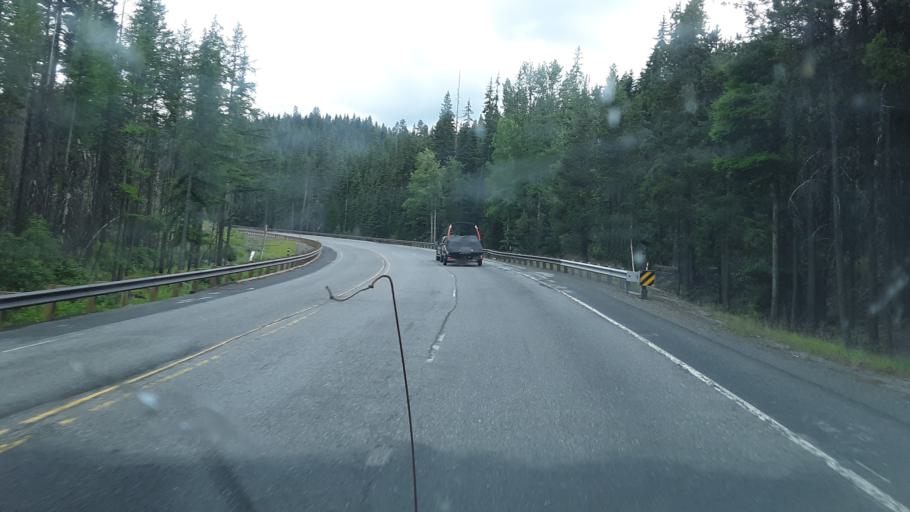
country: US
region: Washington
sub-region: Chelan County
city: Cashmere
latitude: 47.3512
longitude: -120.5710
